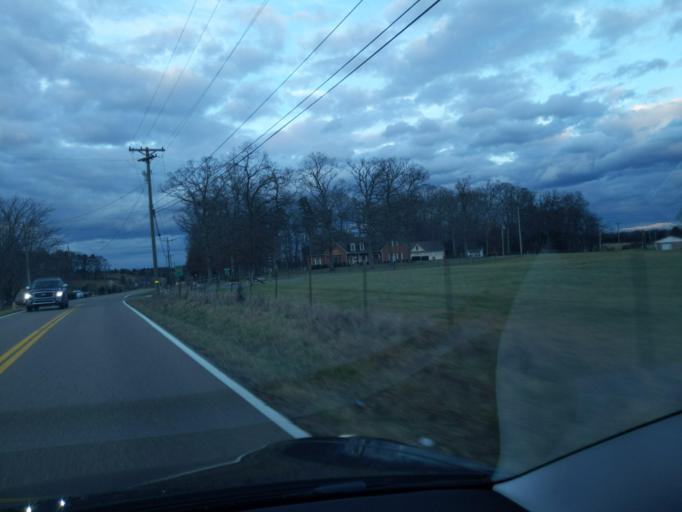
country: US
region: Tennessee
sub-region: Jefferson County
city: White Pine
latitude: 36.0967
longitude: -83.3568
